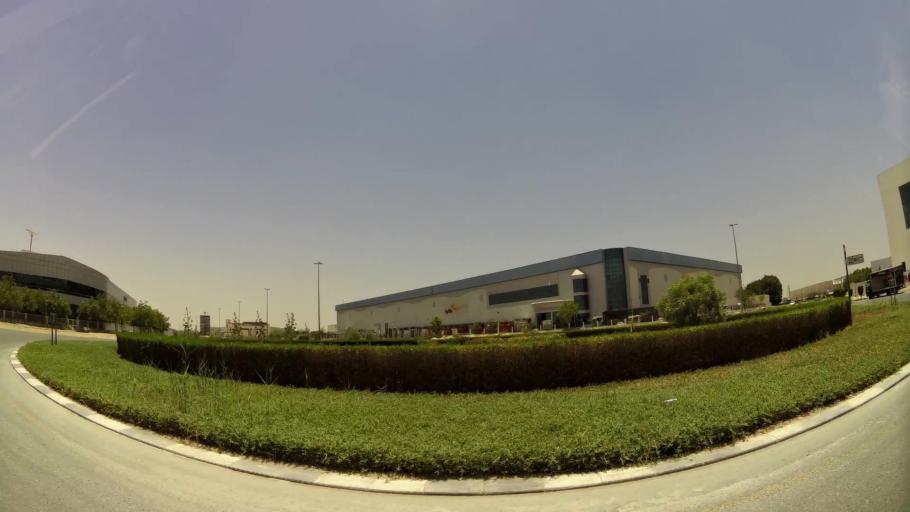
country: AE
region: Dubai
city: Dubai
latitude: 24.9823
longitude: 55.1727
